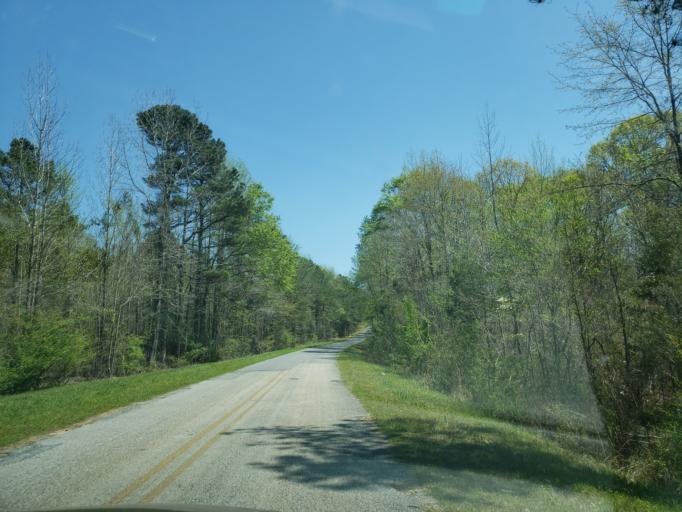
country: US
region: Alabama
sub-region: Tallapoosa County
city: Camp Hill
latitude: 32.6681
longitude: -85.7186
